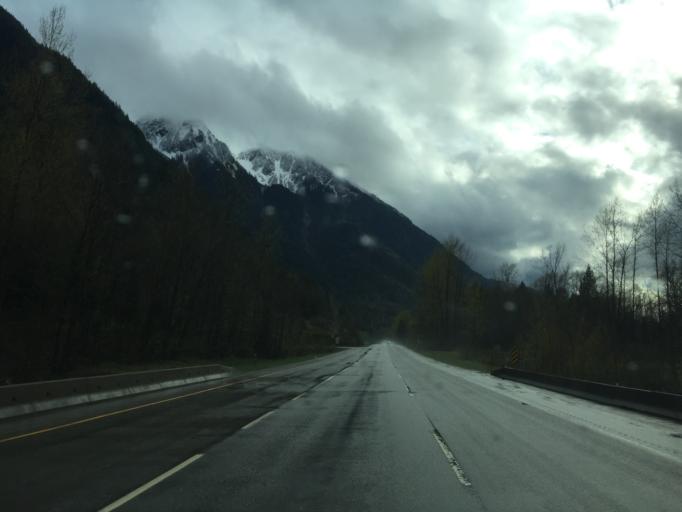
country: CA
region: British Columbia
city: Agassiz
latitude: 49.2285
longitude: -121.6853
